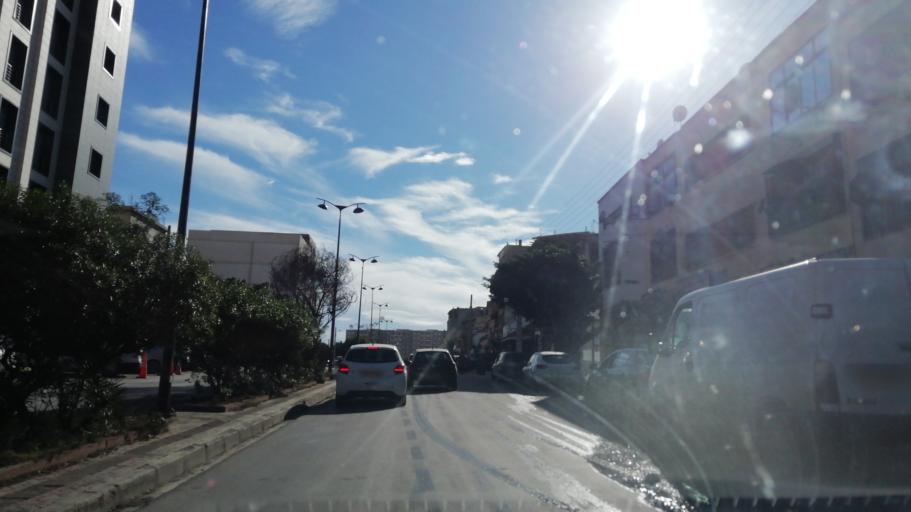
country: DZ
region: Oran
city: Oran
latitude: 35.6931
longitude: -0.6202
